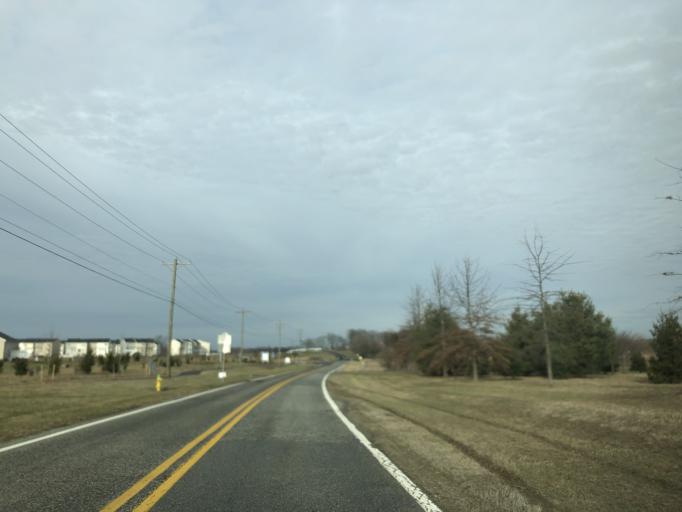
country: US
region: Delaware
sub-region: New Castle County
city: Delaware City
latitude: 39.5202
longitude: -75.6574
